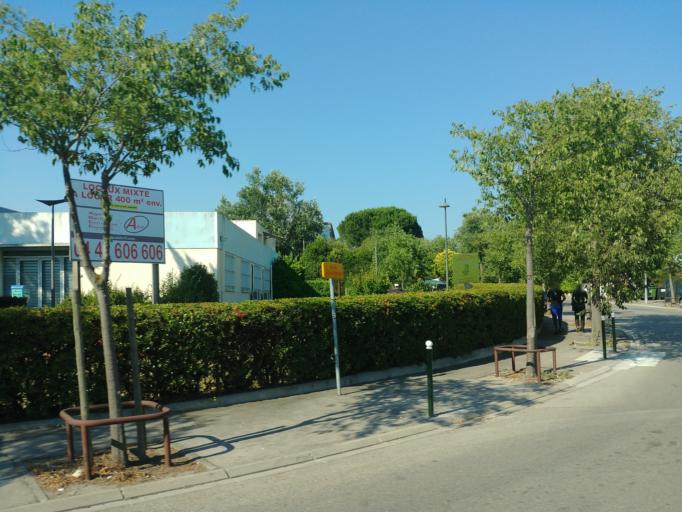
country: FR
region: Provence-Alpes-Cote d'Azur
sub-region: Departement des Bouches-du-Rhone
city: Cabries
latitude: 43.4869
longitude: 5.3791
